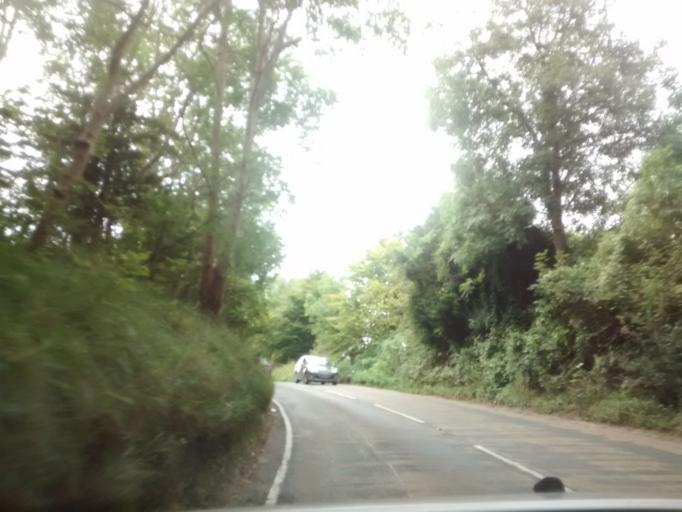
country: GB
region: England
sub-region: South Gloucestershire
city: Cold Ashton
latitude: 51.4312
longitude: -2.4027
